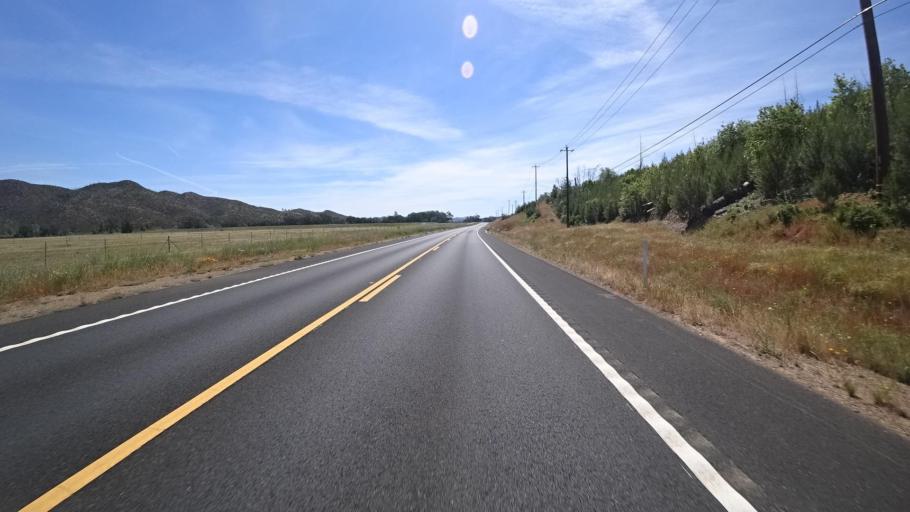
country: US
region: California
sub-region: Lake County
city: Middletown
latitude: 38.7668
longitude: -122.6541
